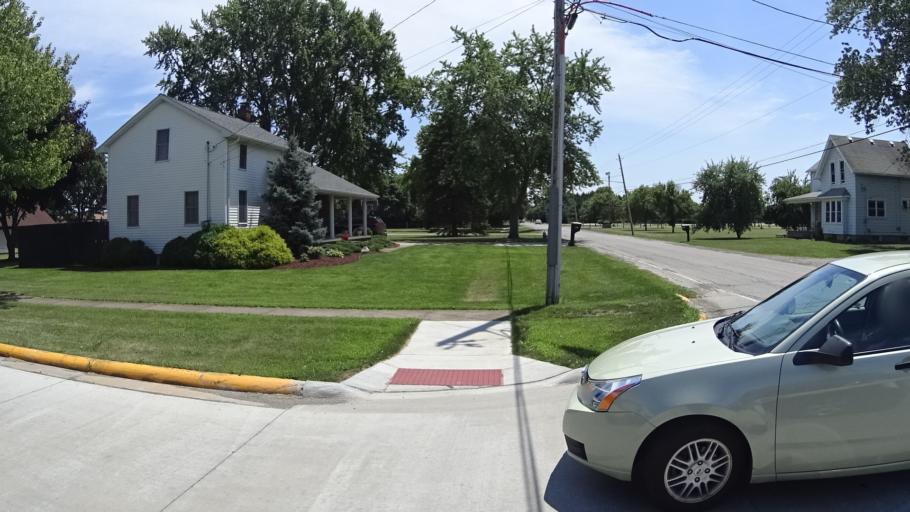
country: US
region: Ohio
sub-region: Erie County
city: Sandusky
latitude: 41.4406
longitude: -82.7726
